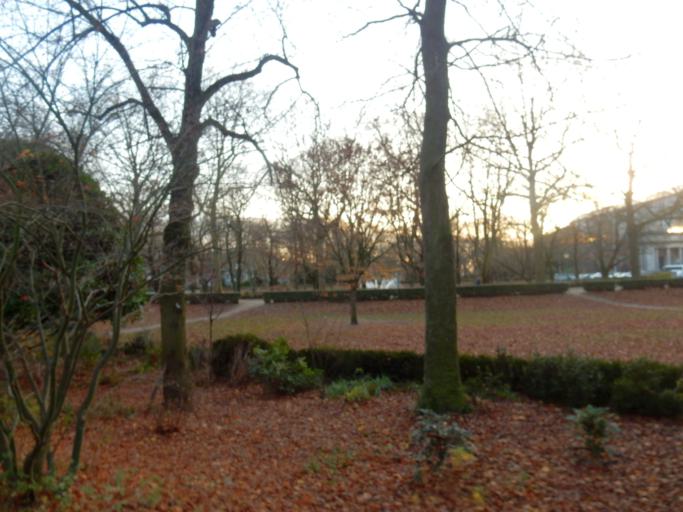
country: BE
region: Brussels Capital
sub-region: Bruxelles-Capitale
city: Brussels
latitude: 50.8413
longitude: 4.3964
